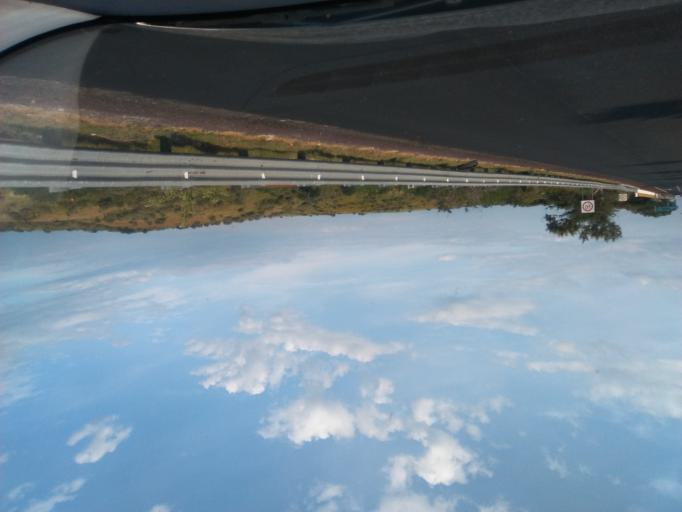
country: MX
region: Morelos
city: Ahuehuetzingo
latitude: 18.6512
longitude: -99.2953
